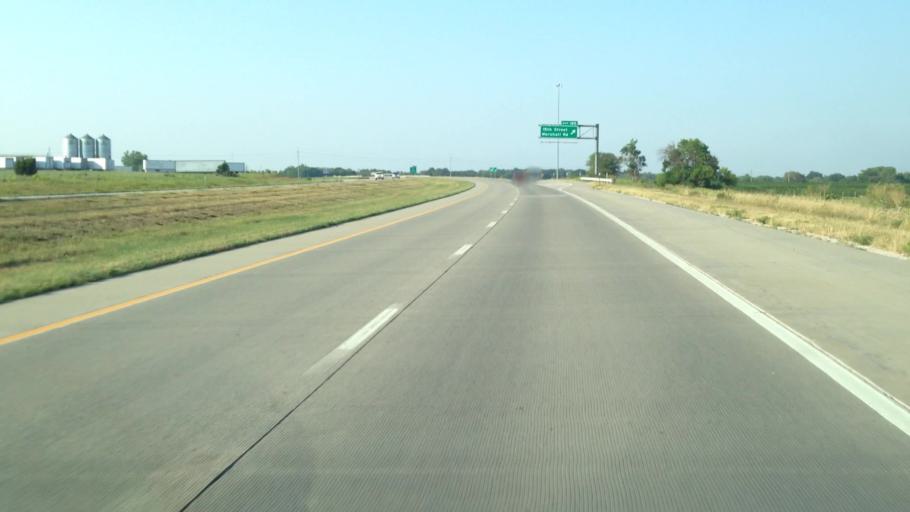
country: US
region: Kansas
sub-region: Franklin County
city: Ottawa
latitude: 38.5889
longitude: -95.2367
